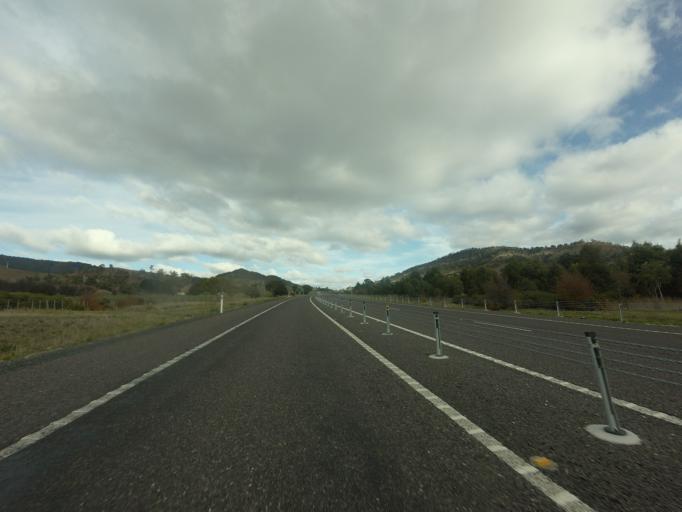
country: AU
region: Tasmania
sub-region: Brighton
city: Bridgewater
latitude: -42.5361
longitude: 147.2060
